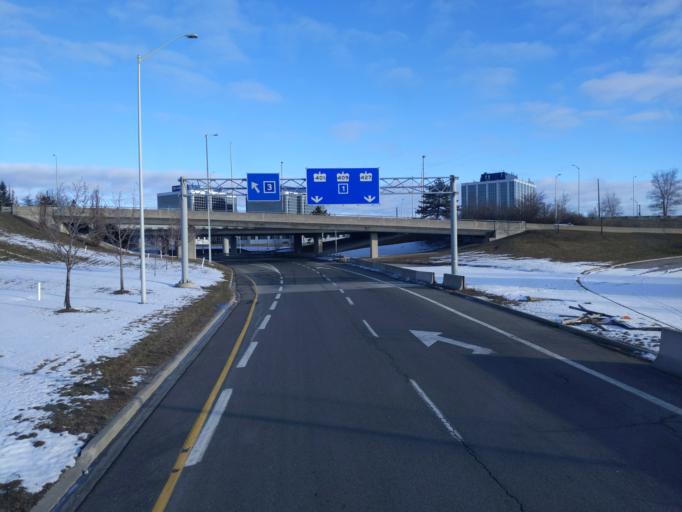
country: CA
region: Ontario
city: Etobicoke
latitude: 43.6844
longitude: -79.6096
